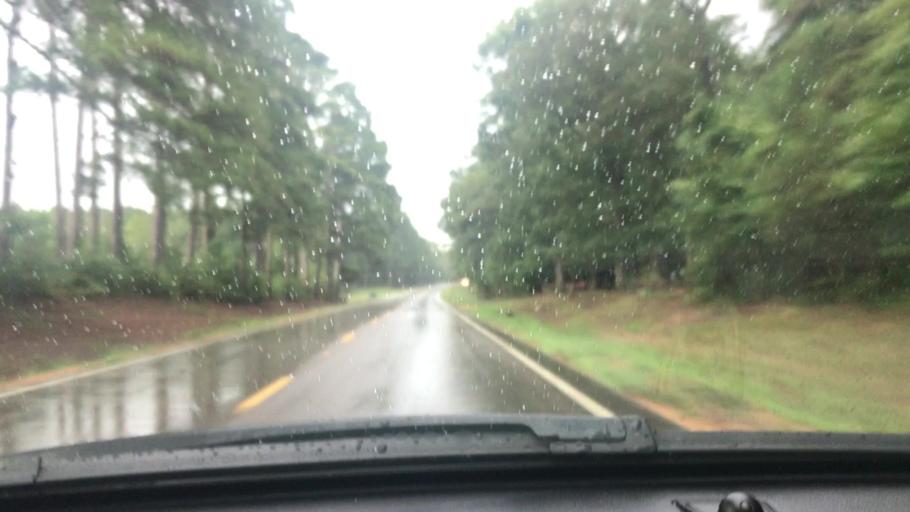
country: US
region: Mississippi
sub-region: Pike County
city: Summit
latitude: 31.3381
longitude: -90.5712
